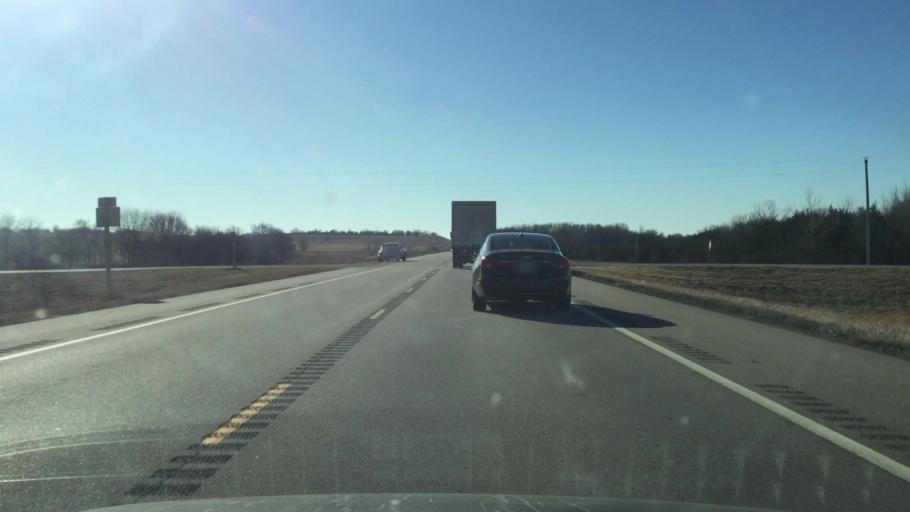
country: US
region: Kansas
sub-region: Allen County
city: Iola
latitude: 38.0248
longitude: -95.3809
